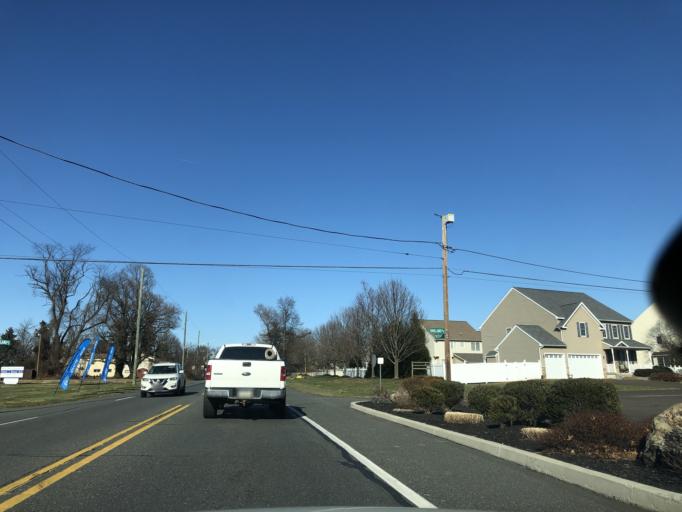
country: US
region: Pennsylvania
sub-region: Bucks County
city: Hulmeville
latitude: 40.1432
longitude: -74.8886
